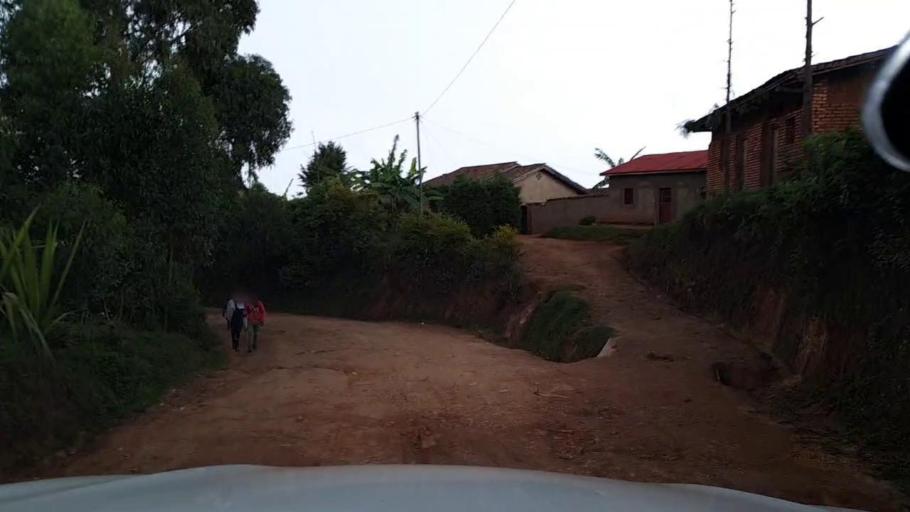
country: BI
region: Kayanza
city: Kayanza
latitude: -2.7878
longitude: 29.5302
